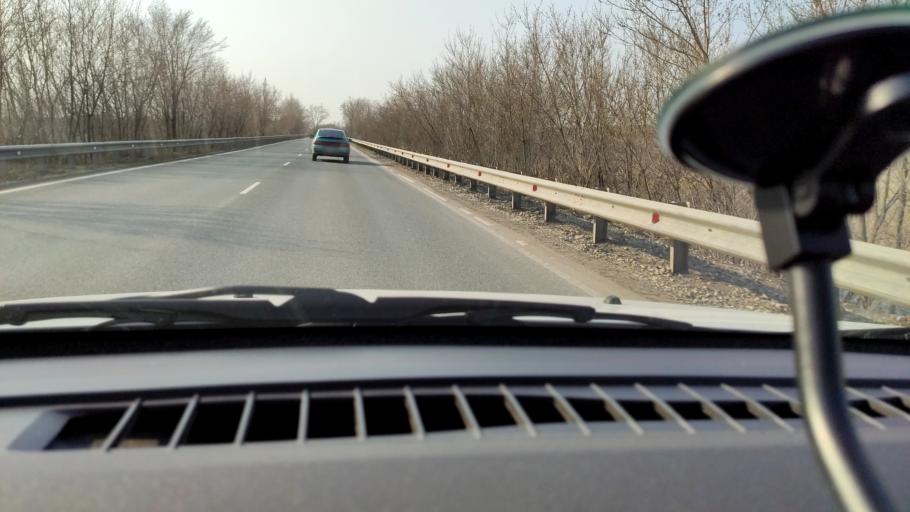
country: RU
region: Samara
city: Samara
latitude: 53.1067
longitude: 50.2416
